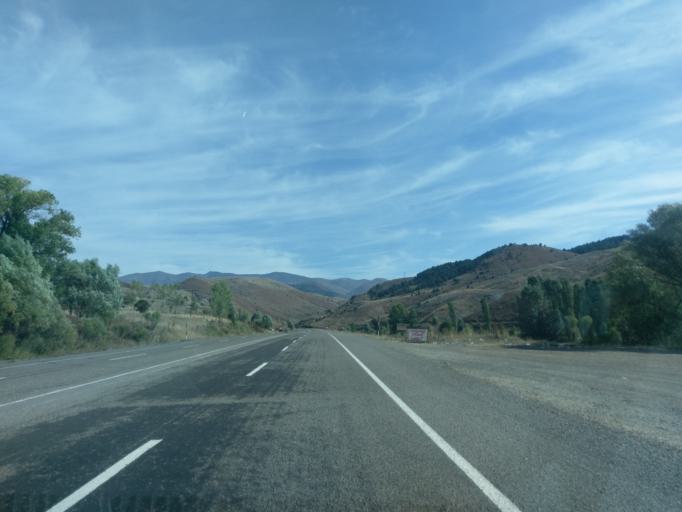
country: TR
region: Sivas
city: Imranli
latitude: 39.8455
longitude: 38.2897
